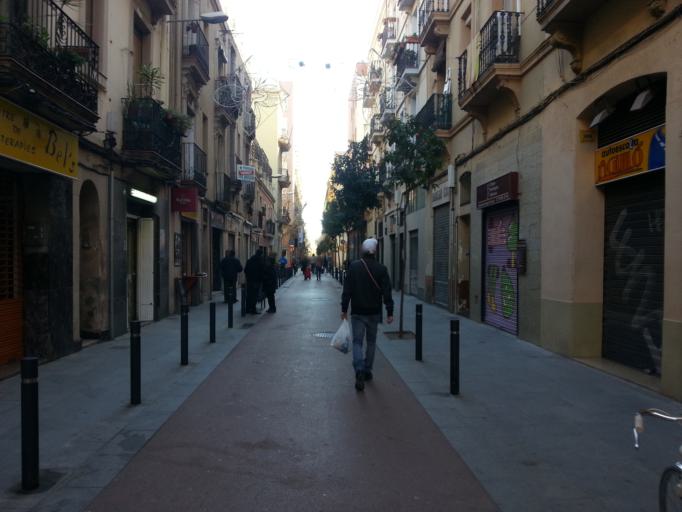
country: ES
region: Catalonia
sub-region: Provincia de Barcelona
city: Sant Marti
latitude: 41.4019
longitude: 2.2020
